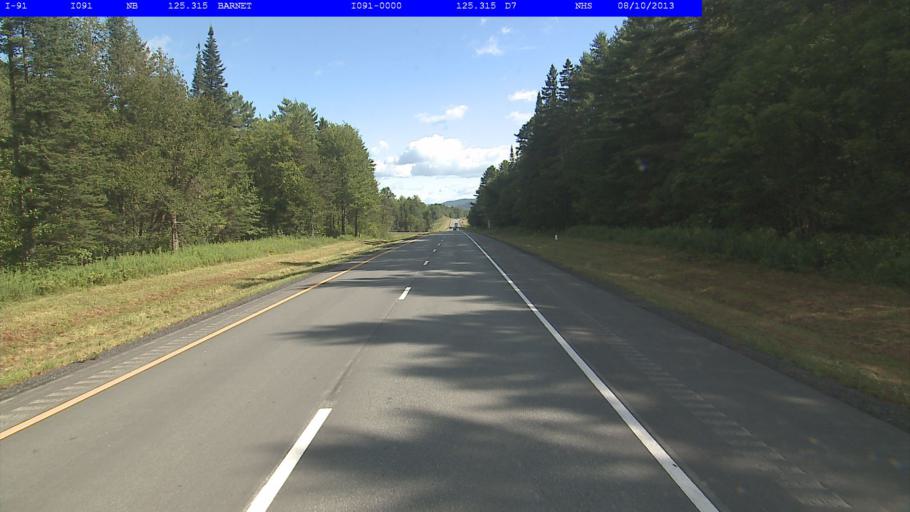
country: US
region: Vermont
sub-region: Caledonia County
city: Saint Johnsbury
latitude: 44.3565
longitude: -72.0333
